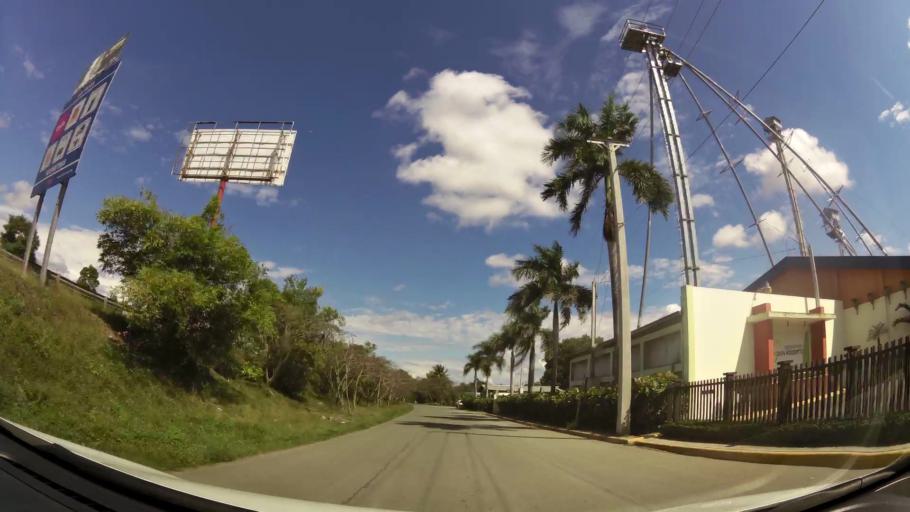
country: DO
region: La Vega
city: Concepcion de La Vega
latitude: 19.2458
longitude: -70.5415
